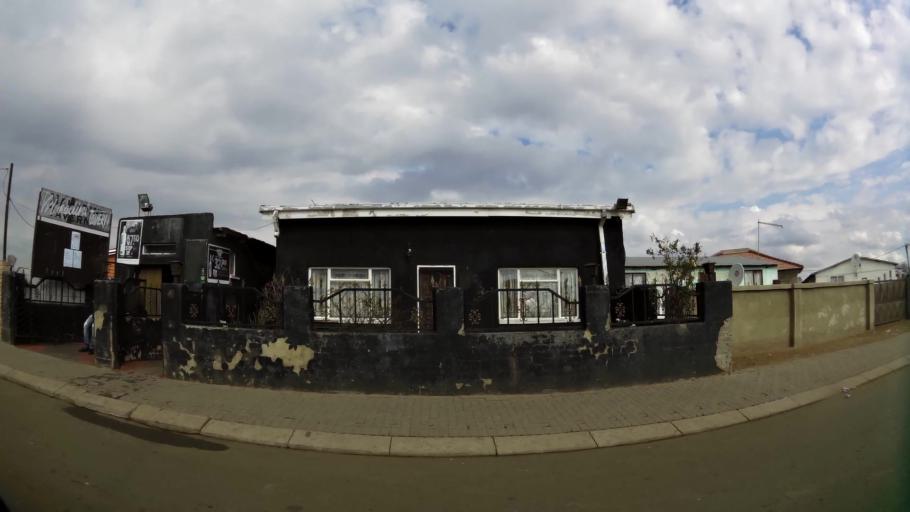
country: ZA
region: Gauteng
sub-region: Sedibeng District Municipality
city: Vanderbijlpark
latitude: -26.6972
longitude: 27.7940
